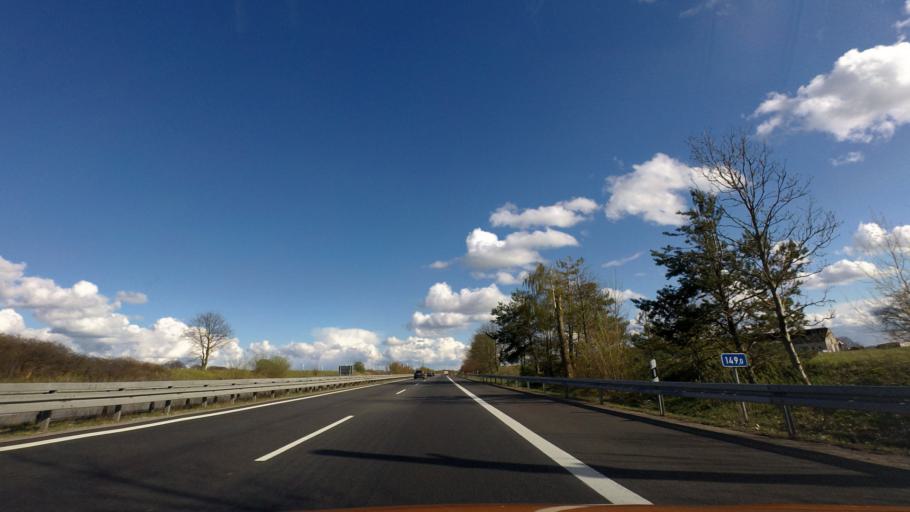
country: DE
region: Brandenburg
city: Gerdshagen
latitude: 53.2543
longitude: 12.1670
